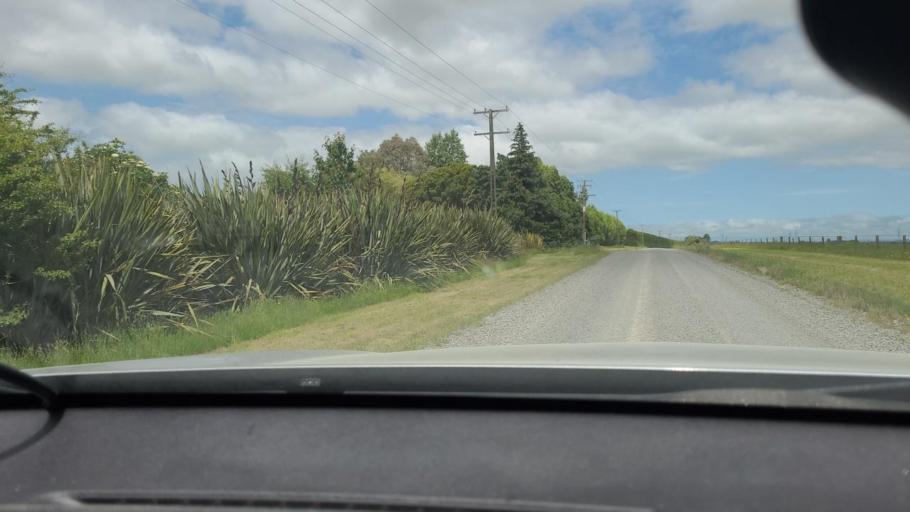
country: NZ
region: Southland
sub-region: Southland District
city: Winton
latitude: -46.0344
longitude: 168.0563
